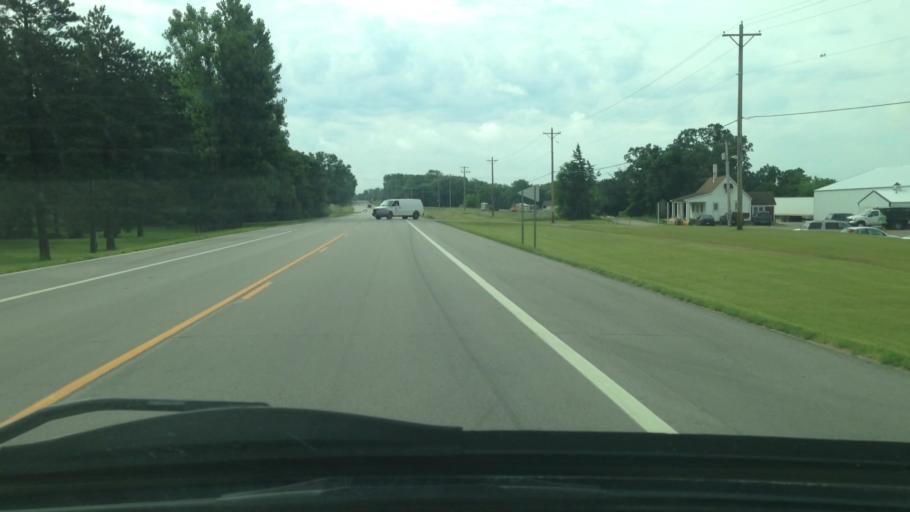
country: US
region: Minnesota
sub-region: Olmsted County
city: Rochester
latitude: 43.9826
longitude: -92.4011
